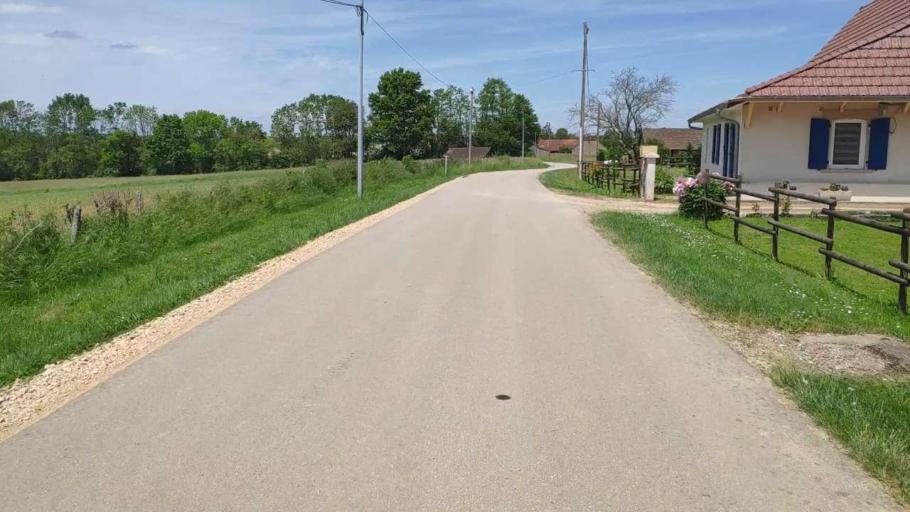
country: FR
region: Franche-Comte
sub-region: Departement du Jura
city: Bletterans
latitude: 46.7970
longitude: 5.3783
